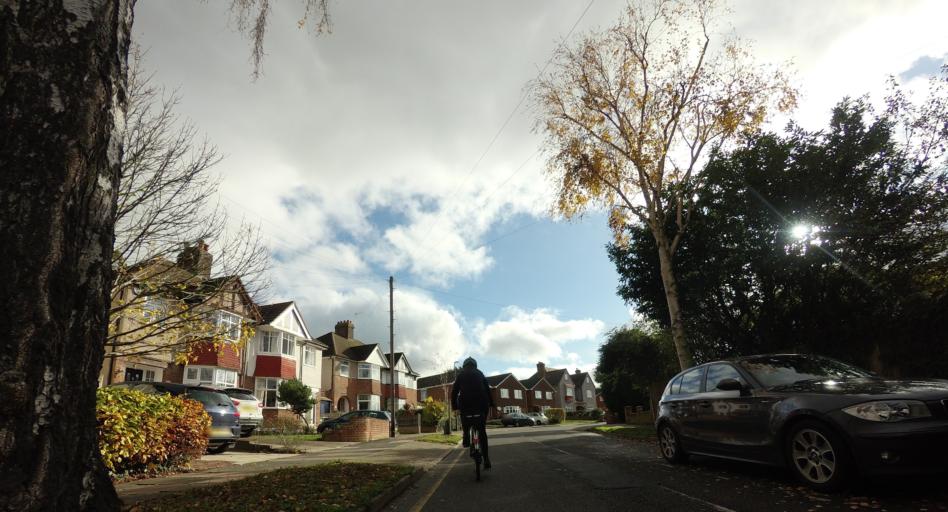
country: GB
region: England
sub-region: Greater London
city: Sidcup
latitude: 51.4320
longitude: 0.1132
